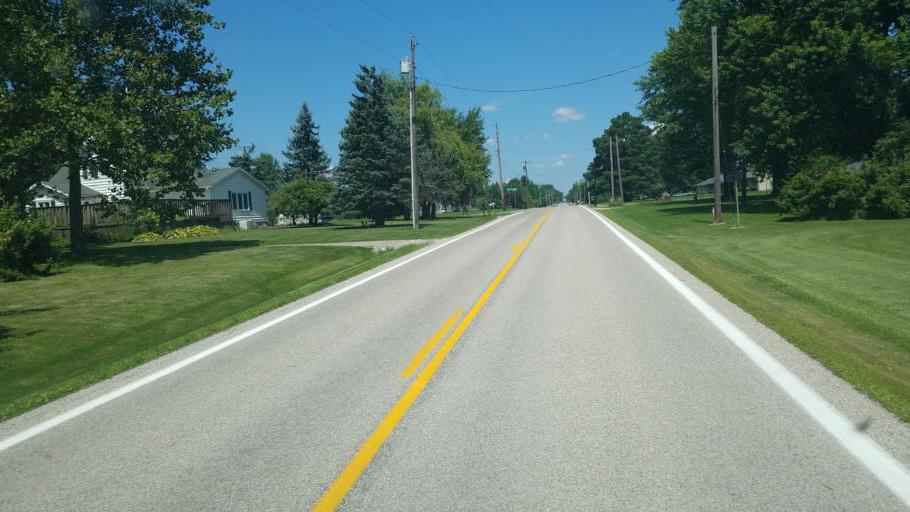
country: US
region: Ohio
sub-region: Marion County
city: Marion
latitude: 40.6072
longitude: -83.2174
